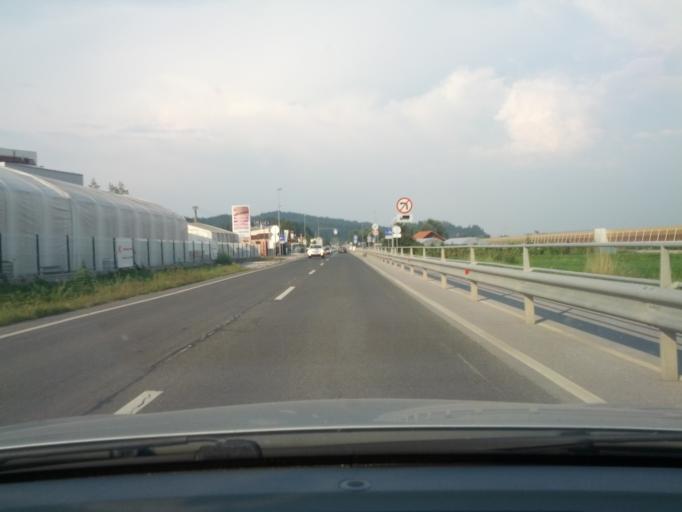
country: SI
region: Log-Dragomer
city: Log pri Brezovici
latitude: 45.9988
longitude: 14.3384
